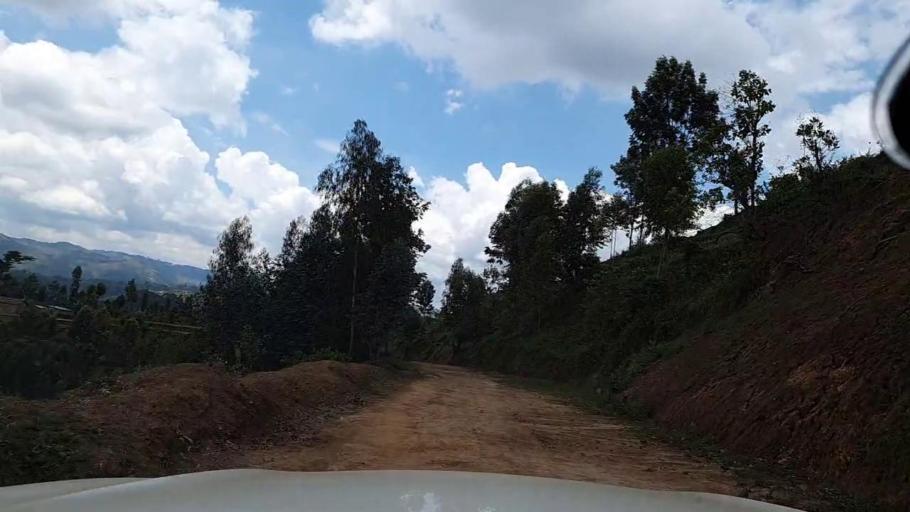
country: RW
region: Southern Province
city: Nzega
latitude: -2.6370
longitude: 29.4868
